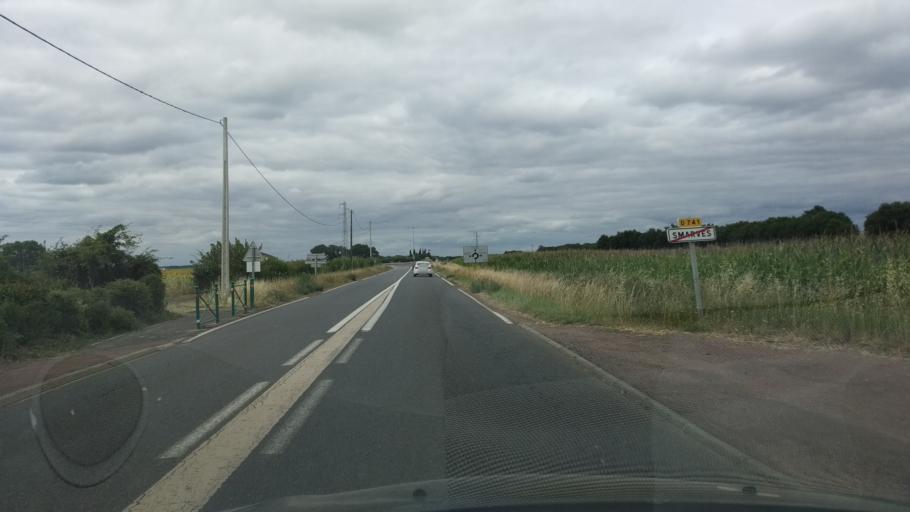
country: FR
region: Poitou-Charentes
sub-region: Departement de la Vienne
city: Smarves
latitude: 46.5157
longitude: 0.3576
